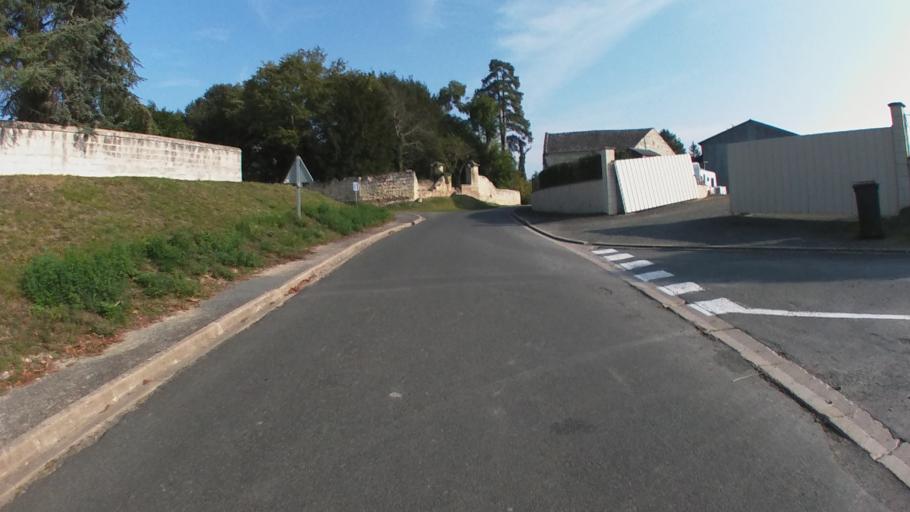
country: FR
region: Pays de la Loire
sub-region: Departement de Maine-et-Loire
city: Distre
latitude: 47.2209
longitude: -0.1158
